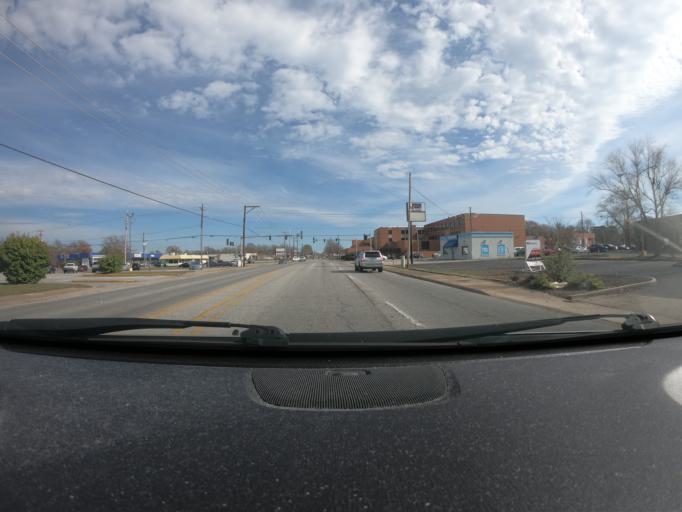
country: US
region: Arkansas
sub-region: Benton County
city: Rogers
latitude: 36.3338
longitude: -94.1360
